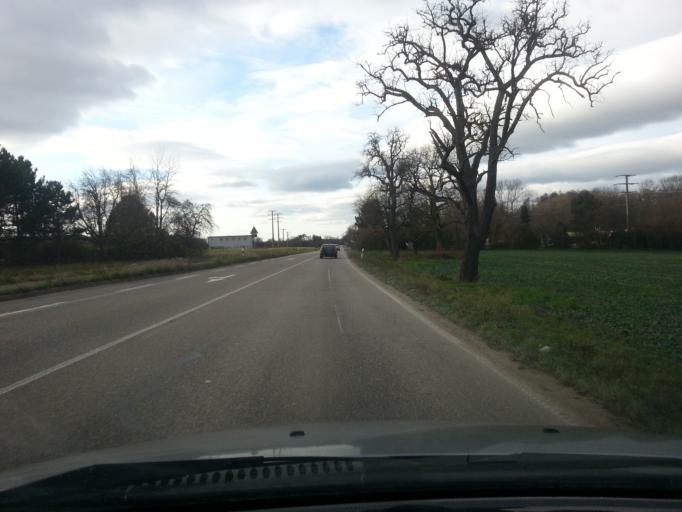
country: DE
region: Baden-Wuerttemberg
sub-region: Karlsruhe Region
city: Ostringen
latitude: 49.2142
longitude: 8.6910
